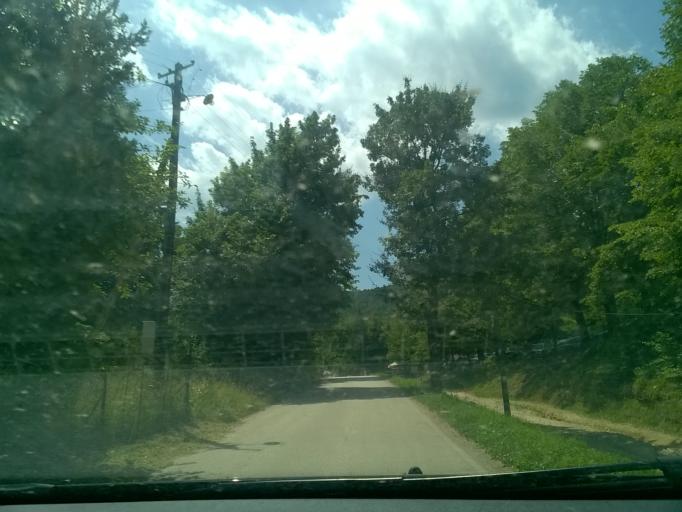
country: RS
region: Central Serbia
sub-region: Zajecarski Okrug
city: Soko Banja
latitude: 43.6245
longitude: 21.8547
